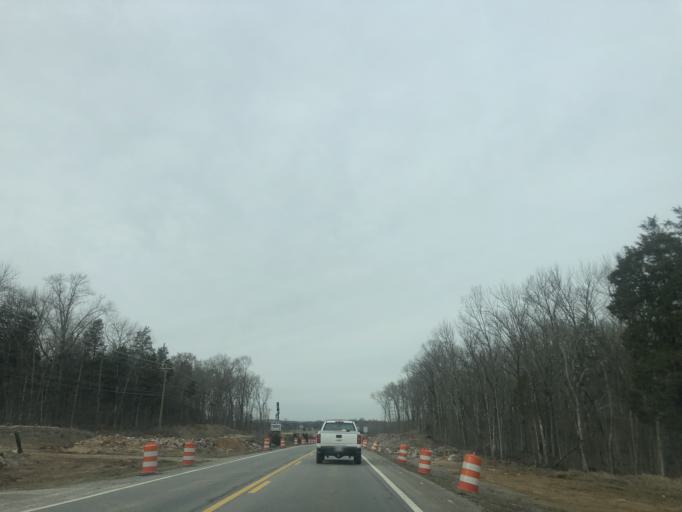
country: US
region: Tennessee
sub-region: Wilson County
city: Mount Juliet
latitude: 36.2738
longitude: -86.4419
